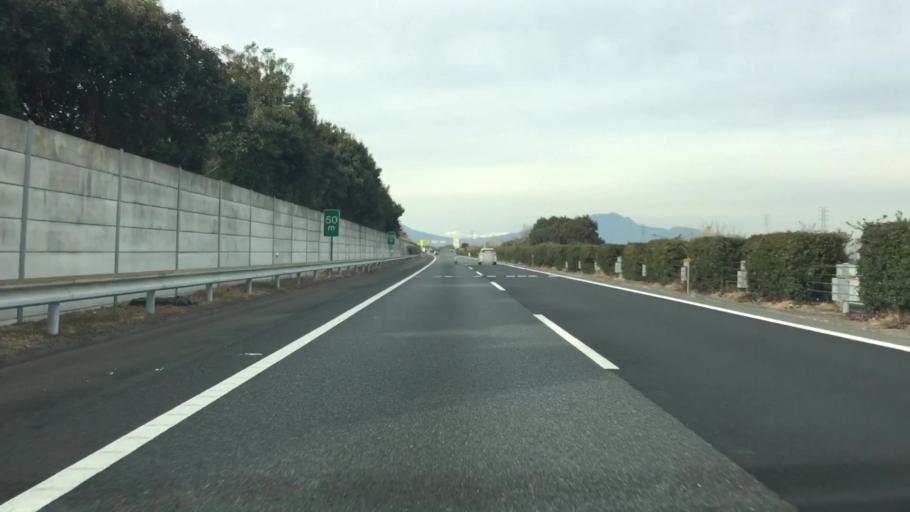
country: JP
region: Gunma
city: Kanekomachi
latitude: 36.4145
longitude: 139.0211
